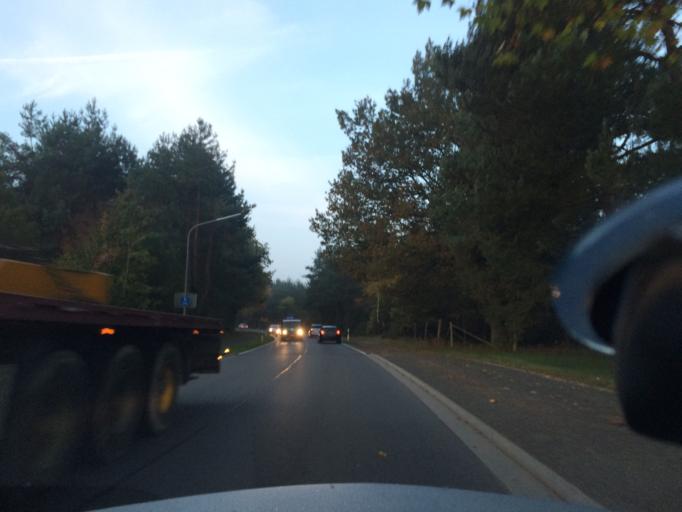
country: DE
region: Hesse
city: Morfelden-Walldorf
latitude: 49.9800
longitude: 8.5513
